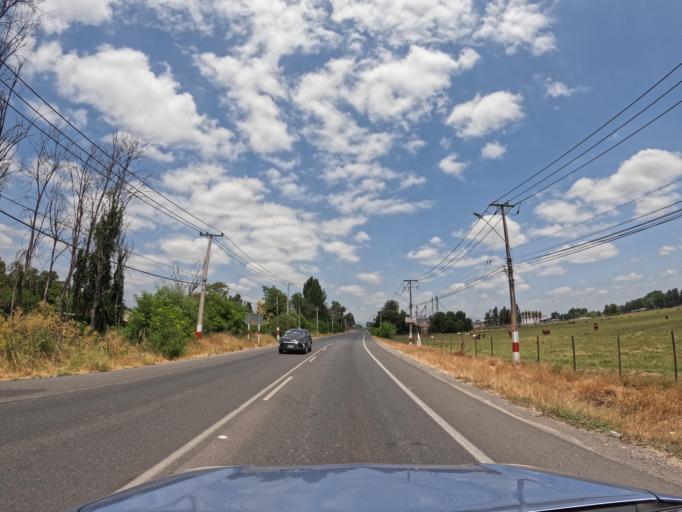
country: CL
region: Maule
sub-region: Provincia de Curico
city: Curico
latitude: -35.0032
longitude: -71.2261
